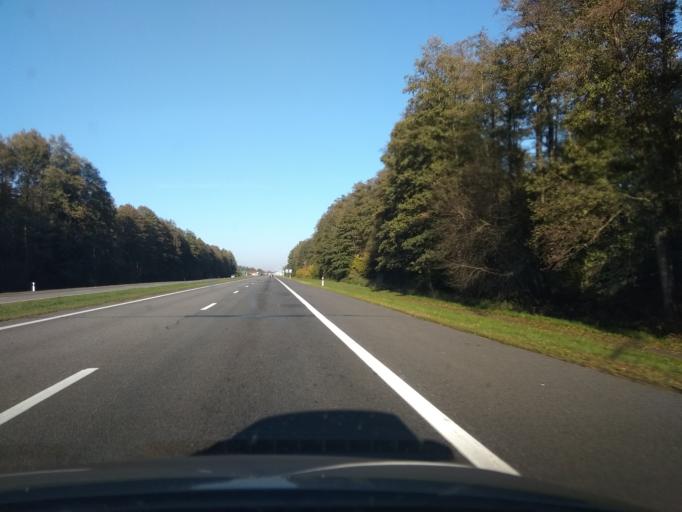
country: BY
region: Brest
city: Ivatsevichy
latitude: 52.6892
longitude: 25.3437
